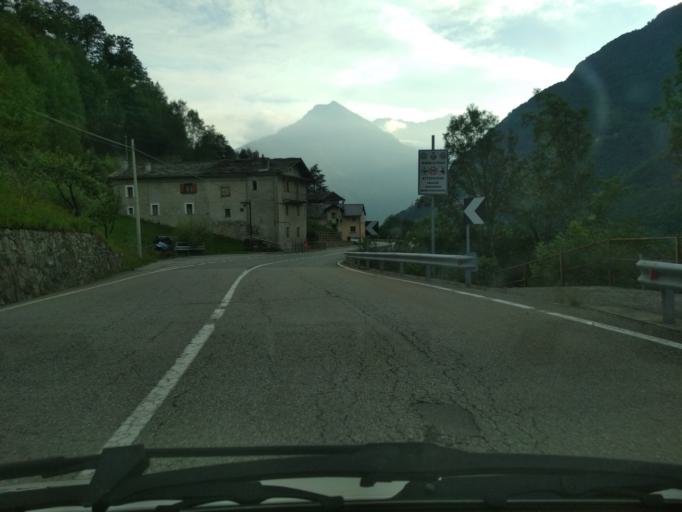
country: IT
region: Aosta Valley
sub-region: Valle d'Aosta
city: Perloz
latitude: 45.6211
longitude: 7.8212
